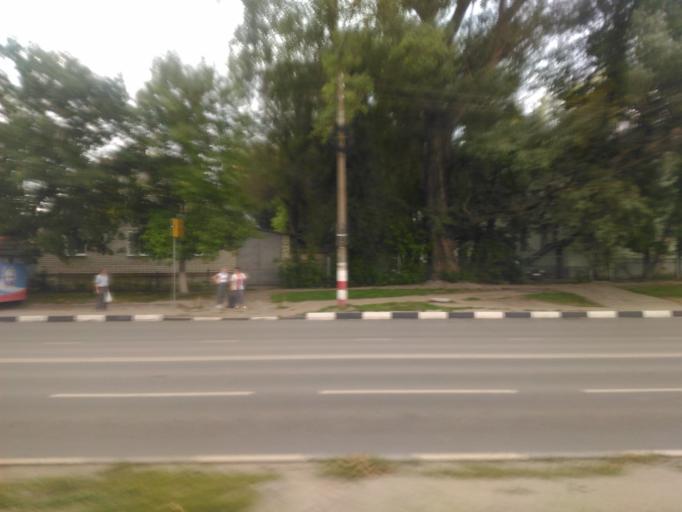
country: RU
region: Ulyanovsk
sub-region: Ulyanovskiy Rayon
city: Ulyanovsk
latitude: 54.2707
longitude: 48.3247
